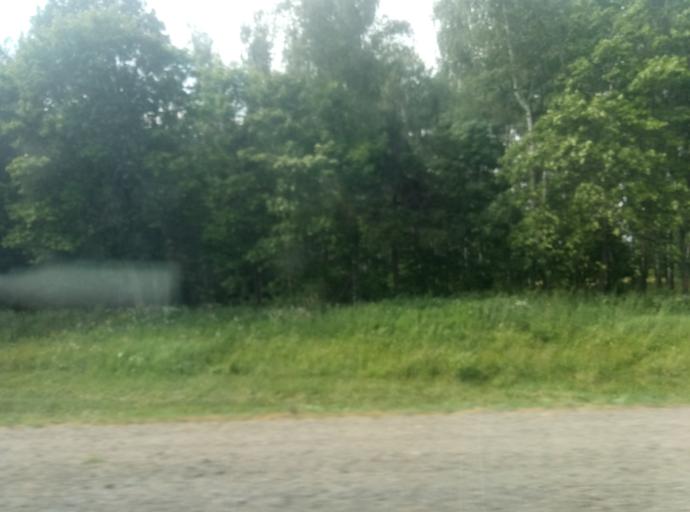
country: RU
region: Tula
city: Bogoroditsk
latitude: 53.8532
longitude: 38.0804
